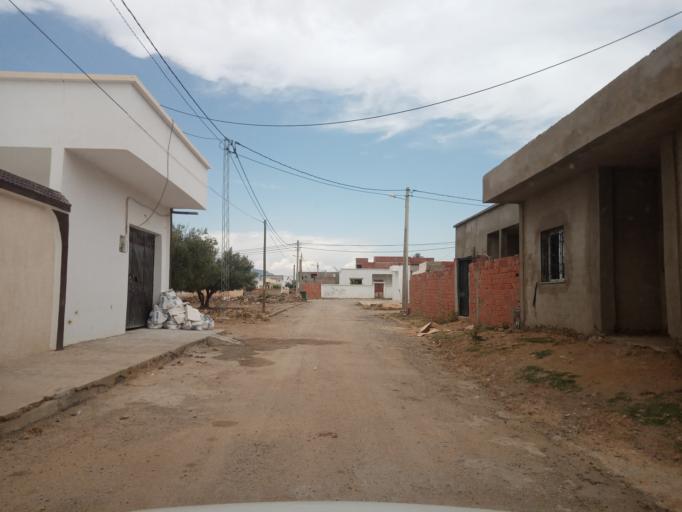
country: TN
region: Al Qayrawan
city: Sbikha
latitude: 36.1141
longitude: 10.0919
